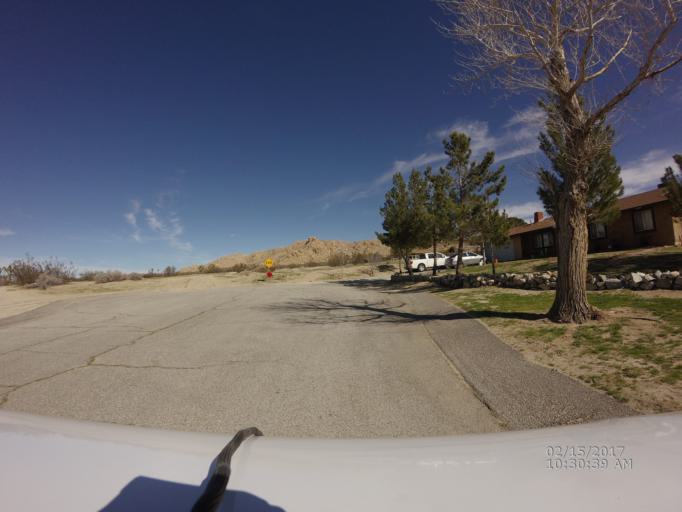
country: US
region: California
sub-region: Los Angeles County
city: Lake Los Angeles
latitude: 34.5852
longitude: -117.8606
